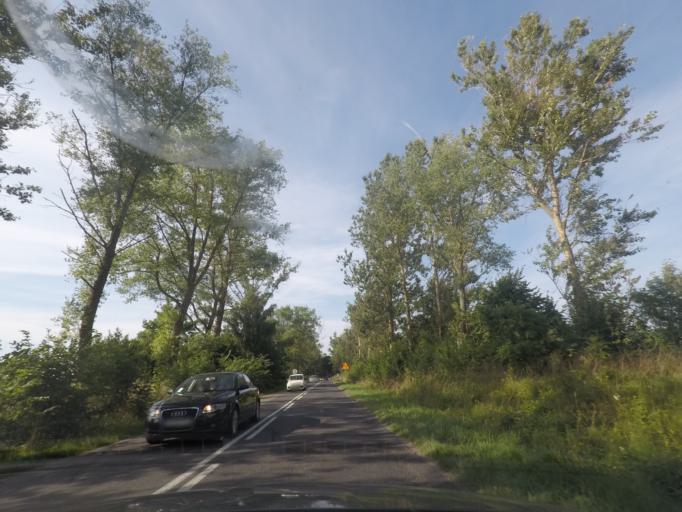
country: PL
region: Pomeranian Voivodeship
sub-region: Powiat leborski
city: Leba
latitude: 54.6856
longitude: 17.5960
